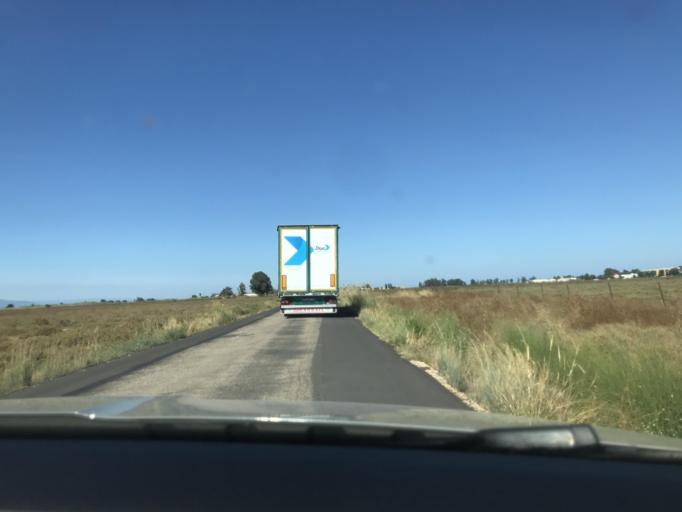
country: ES
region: Catalonia
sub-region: Provincia de Tarragona
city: Deltebre
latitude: 40.6553
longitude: 0.7710
